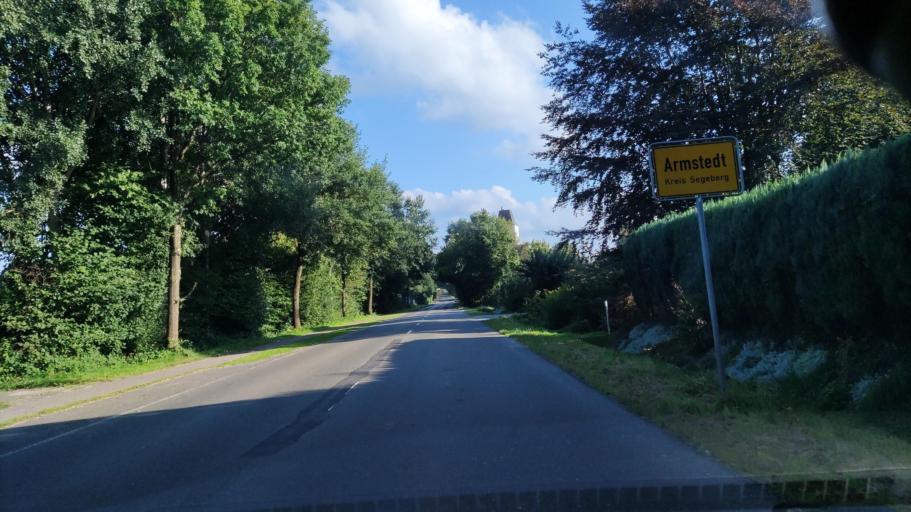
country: DE
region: Schleswig-Holstein
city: Armstedt
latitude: 53.9732
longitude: 9.8451
